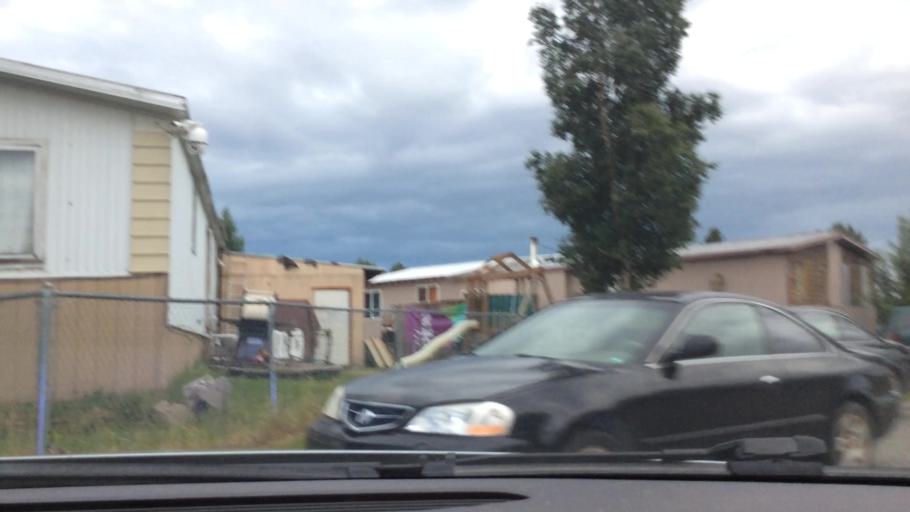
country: US
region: Alaska
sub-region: Anchorage Municipality
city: Anchorage
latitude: 61.1337
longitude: -149.8515
